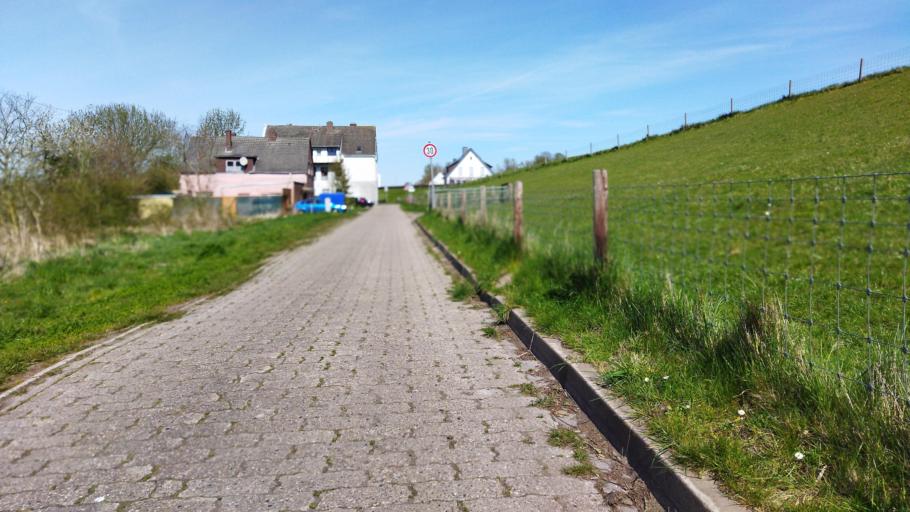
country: DE
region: Lower Saxony
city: Nordenham
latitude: 53.4660
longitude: 8.4763
